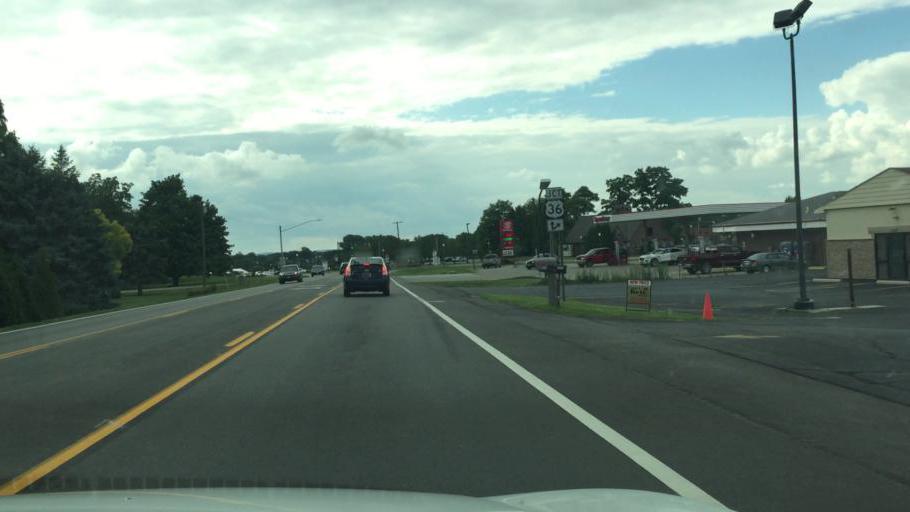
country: US
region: Ohio
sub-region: Champaign County
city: Urbana
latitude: 40.1056
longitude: -83.7269
